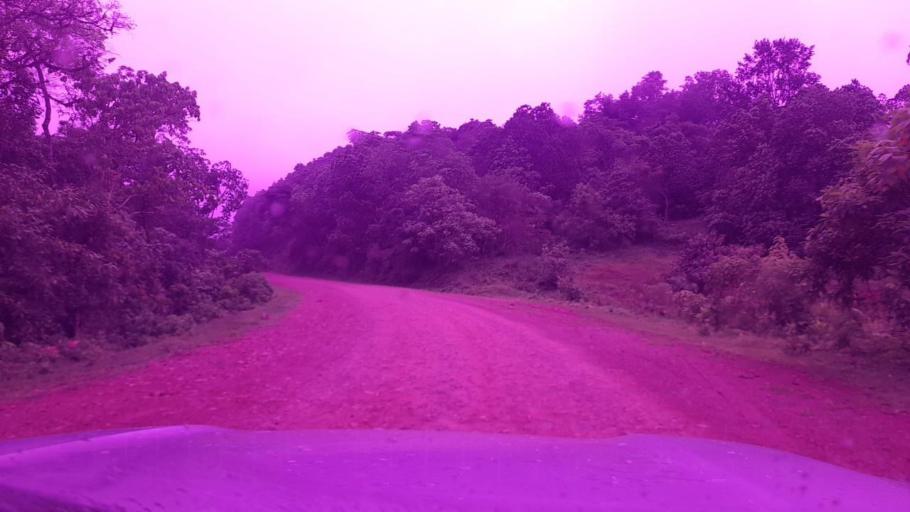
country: ET
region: Southern Nations, Nationalities, and People's Region
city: Bonga
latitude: 7.5202
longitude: 36.0579
